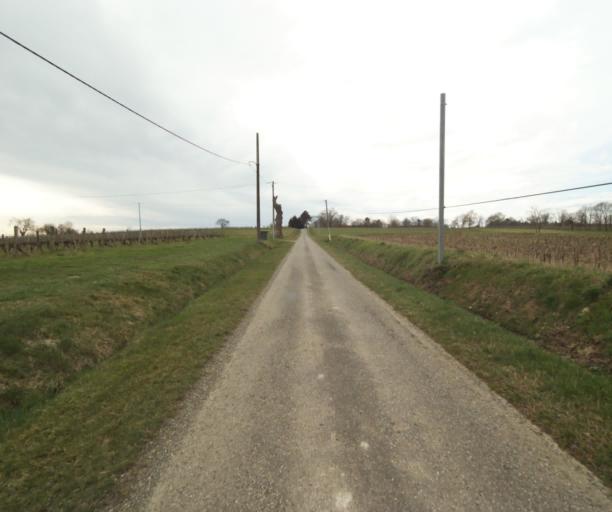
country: FR
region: Midi-Pyrenees
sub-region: Departement du Gers
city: Eauze
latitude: 43.9048
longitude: 0.0467
